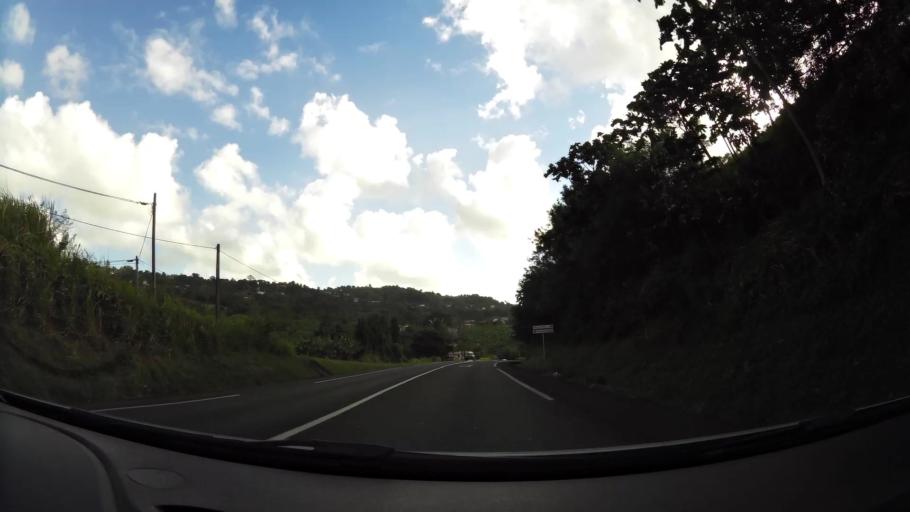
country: MQ
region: Martinique
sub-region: Martinique
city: Ducos
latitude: 14.6014
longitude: -60.9536
